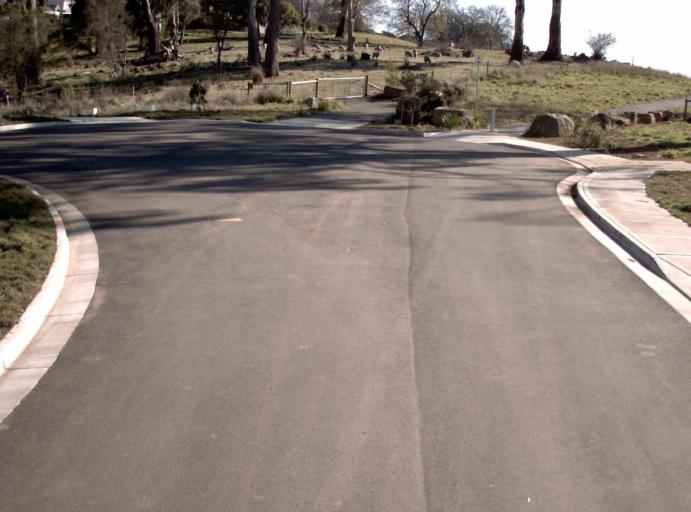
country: AU
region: Tasmania
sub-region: Launceston
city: Summerhill
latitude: -41.4727
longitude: 147.1500
